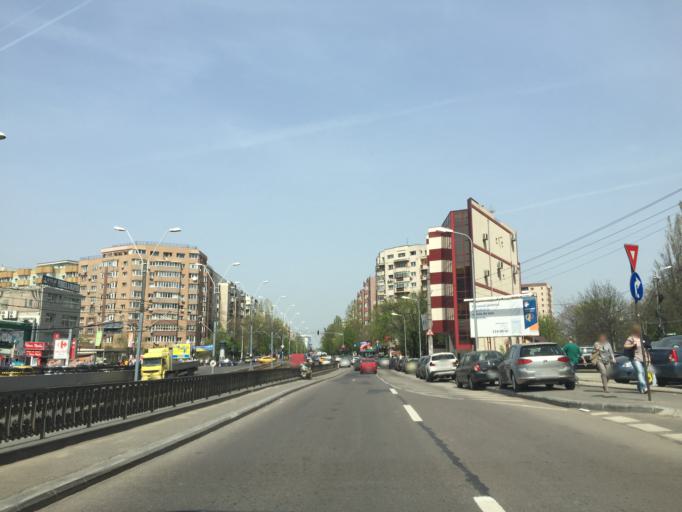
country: RO
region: Ilfov
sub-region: Comuna Chiajna
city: Rosu
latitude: 44.4352
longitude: 26.0352
